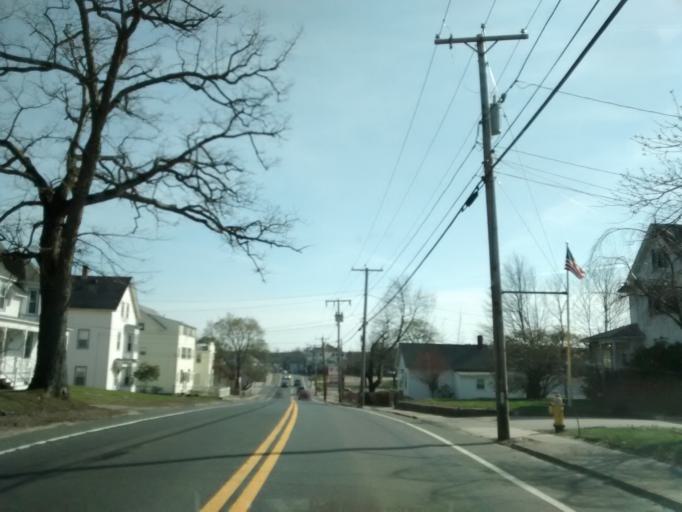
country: US
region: Massachusetts
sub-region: Worcester County
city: Whitinsville
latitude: 42.1018
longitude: -71.6422
